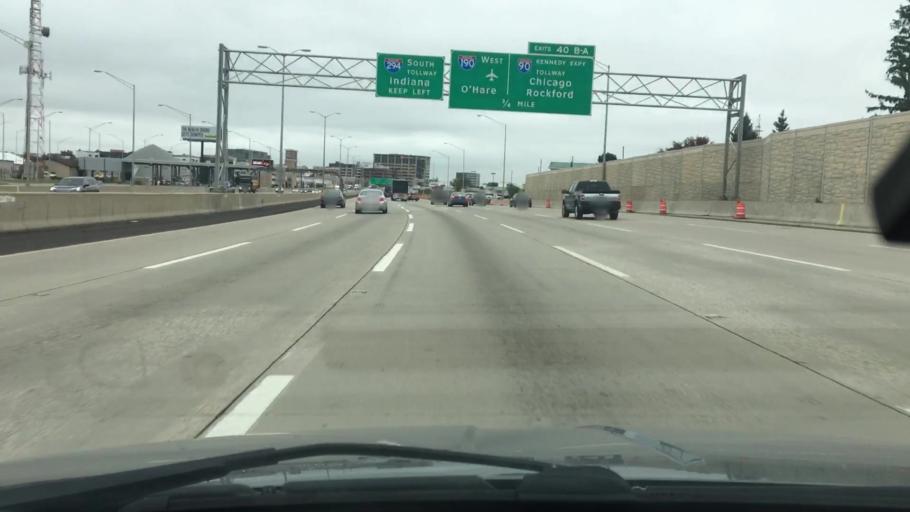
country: US
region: Illinois
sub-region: Cook County
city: Rosemont
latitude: 42.0039
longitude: -87.8683
